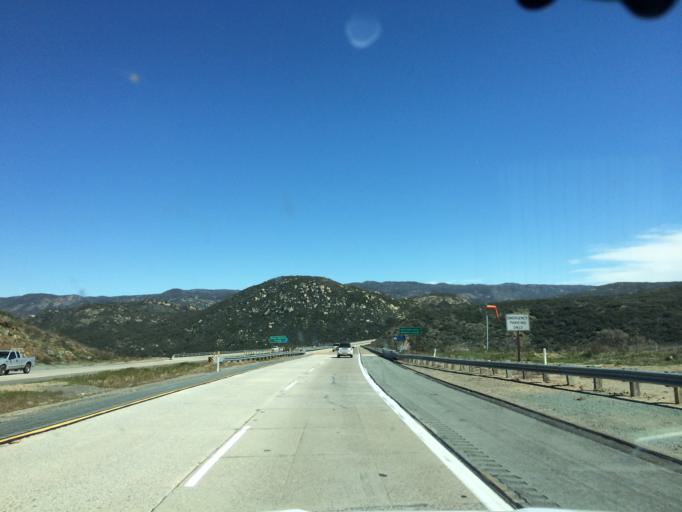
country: US
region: California
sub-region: San Diego County
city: Pine Valley
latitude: 32.8229
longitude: -116.5641
